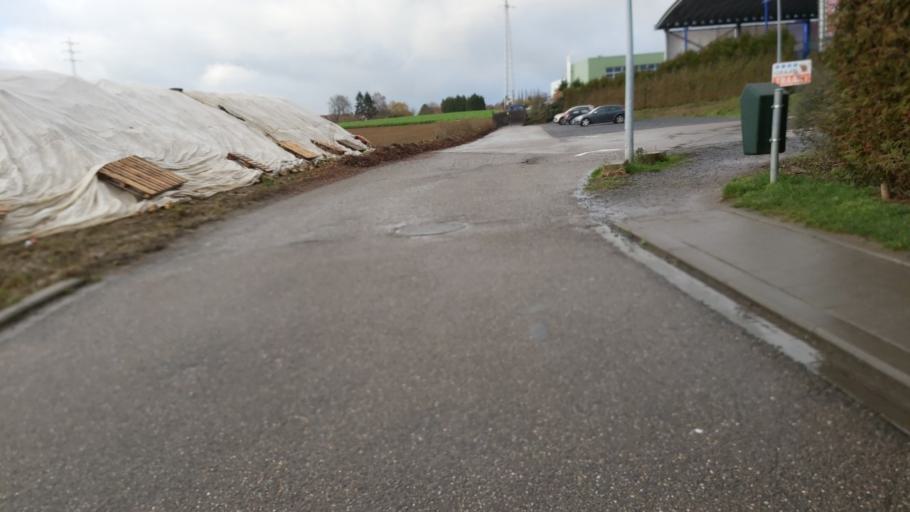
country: BE
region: Flanders
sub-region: Provincie Vlaams-Brabant
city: Tienen
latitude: 50.8173
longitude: 4.9406
